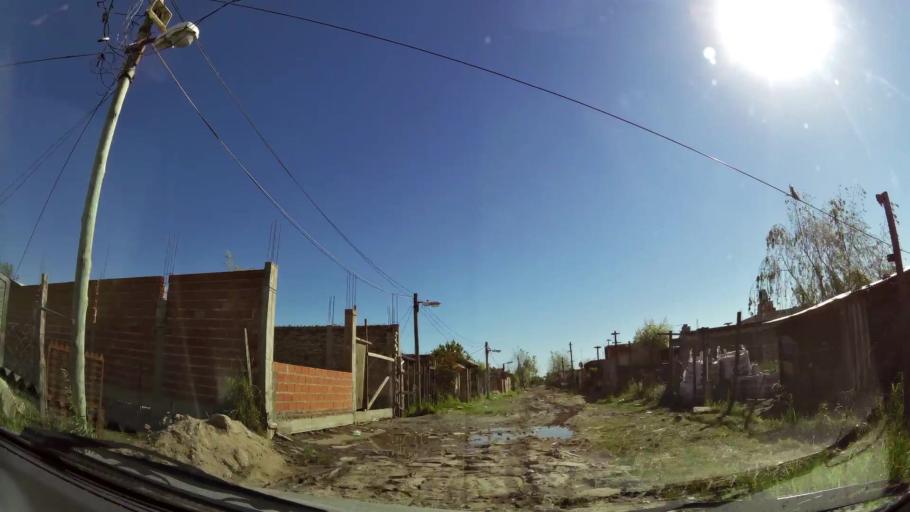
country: AR
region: Buenos Aires
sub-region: Partido de Quilmes
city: Quilmes
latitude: -34.7618
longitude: -58.3093
